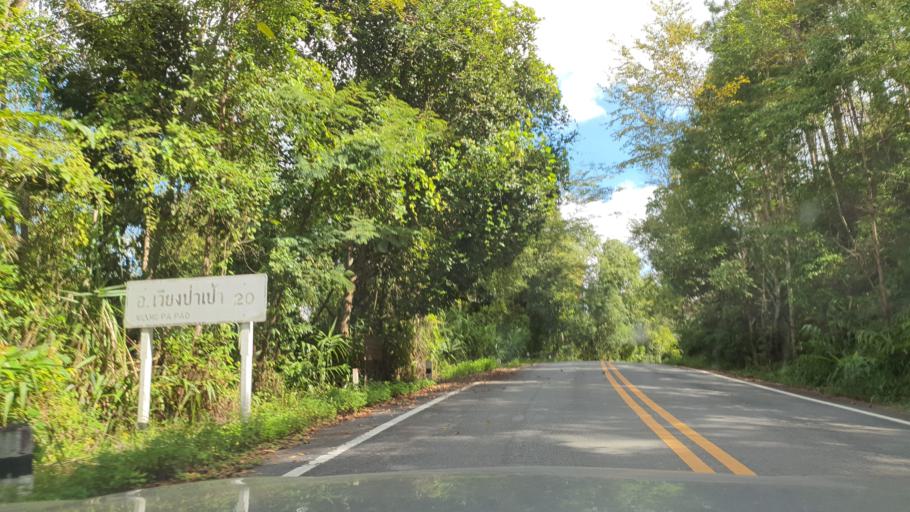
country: TH
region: Chiang Rai
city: Wiang Pa Pao
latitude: 19.3143
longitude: 99.3844
